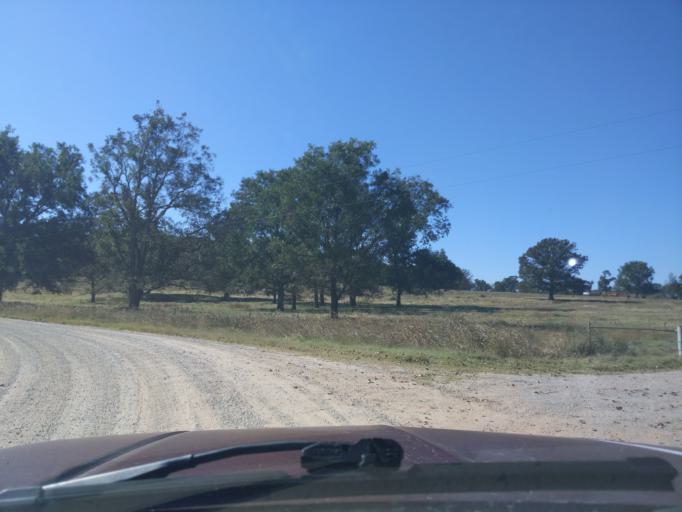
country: US
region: Oklahoma
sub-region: Creek County
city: Bristow
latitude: 35.6827
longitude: -96.4232
